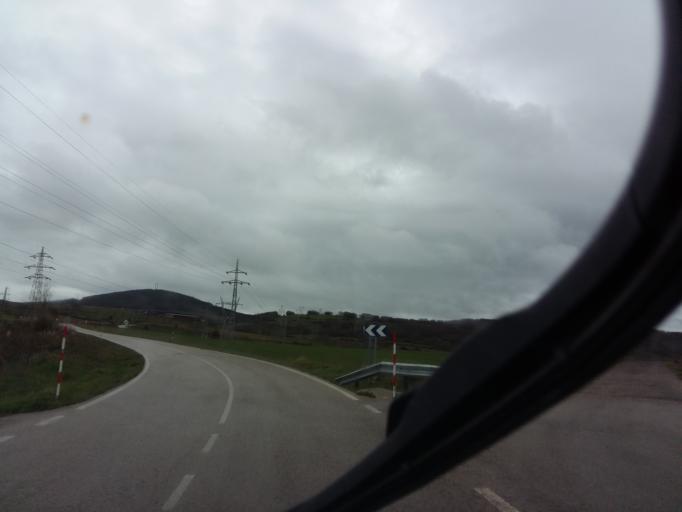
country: ES
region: Cantabria
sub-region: Provincia de Cantabria
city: Mataporquera
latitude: 42.8817
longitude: -4.1582
